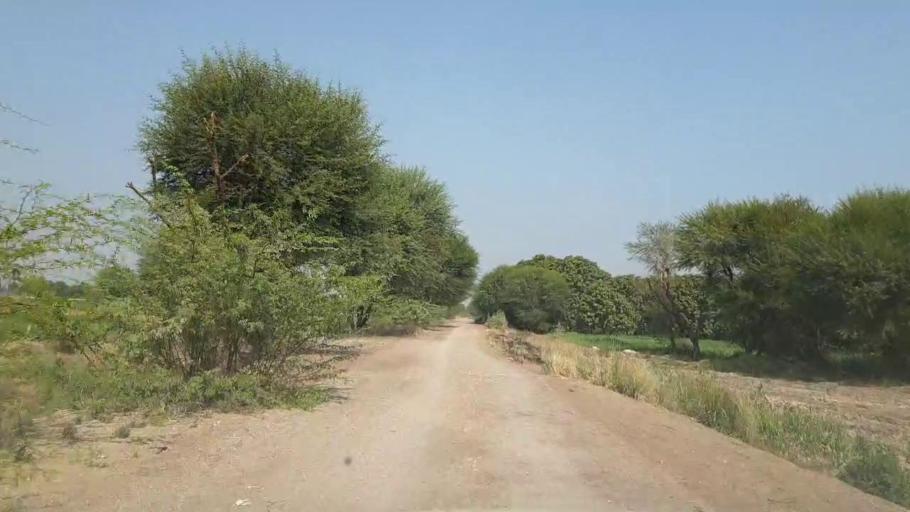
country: PK
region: Sindh
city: Mirpur Khas
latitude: 25.6195
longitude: 69.1029
